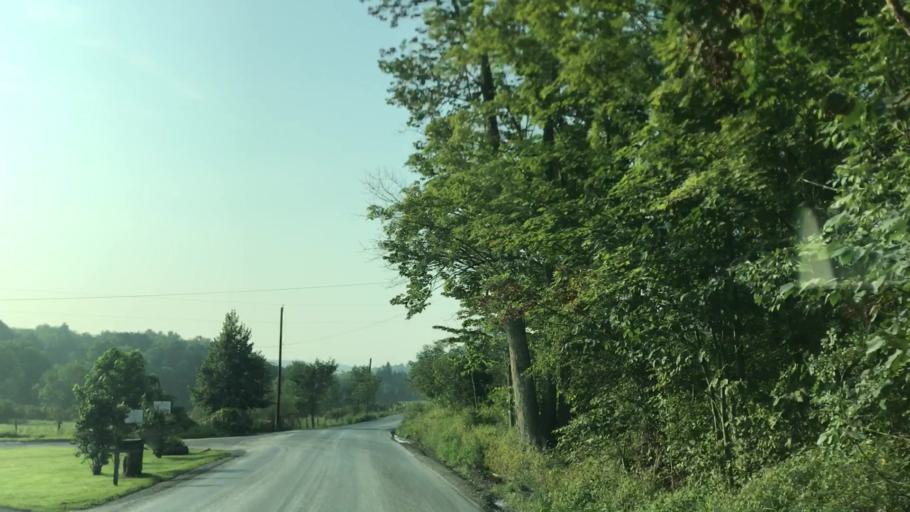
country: US
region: Pennsylvania
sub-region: Wyoming County
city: Factoryville
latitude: 41.6689
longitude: -75.8111
